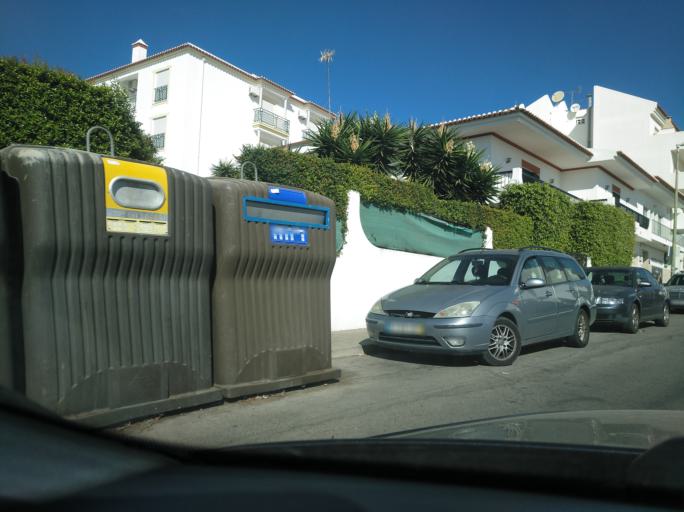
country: PT
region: Faro
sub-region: Vila Real de Santo Antonio
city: Monte Gordo
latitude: 37.1749
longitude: -7.5326
